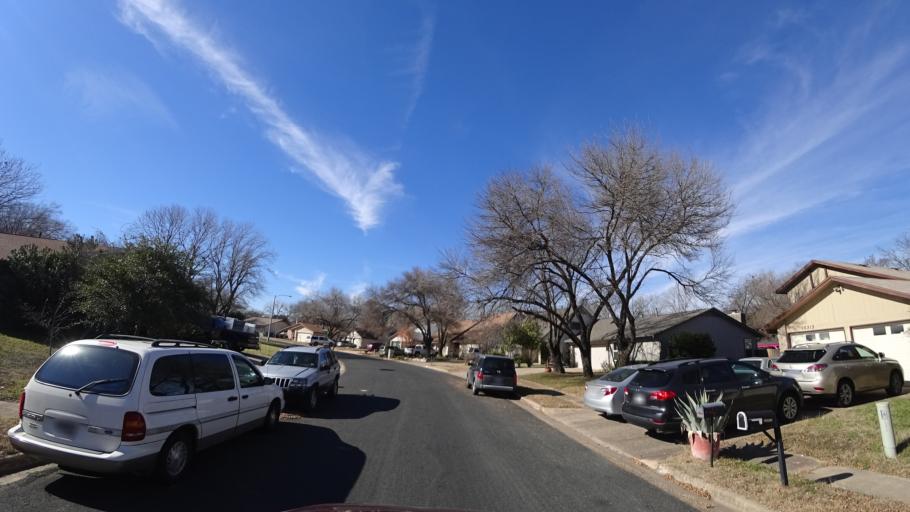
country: US
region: Texas
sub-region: Travis County
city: Wells Branch
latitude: 30.3801
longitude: -97.7092
